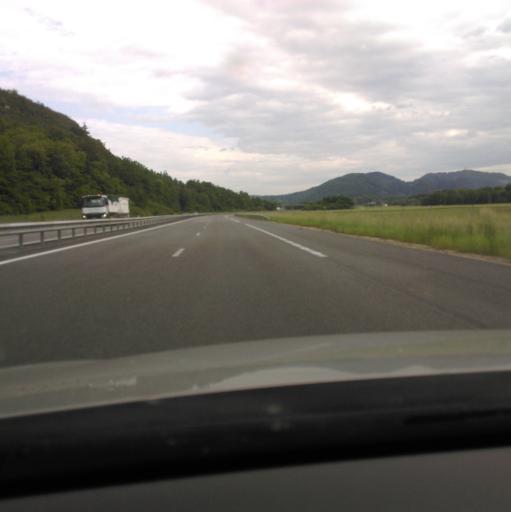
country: FR
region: Rhone-Alpes
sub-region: Departement de l'Ain
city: Saint-Martin-du-Frene
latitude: 46.1506
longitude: 5.5469
